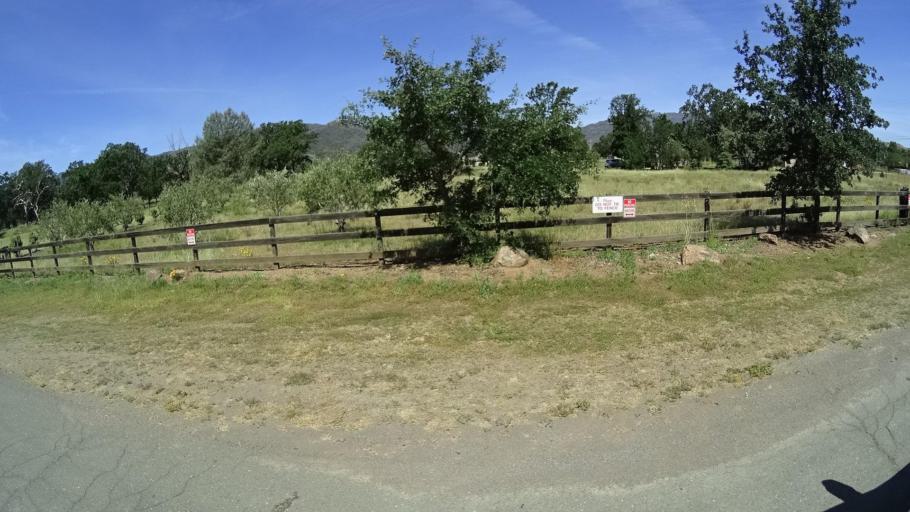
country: US
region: California
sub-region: Lake County
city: Middletown
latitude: 38.7463
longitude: -122.6257
